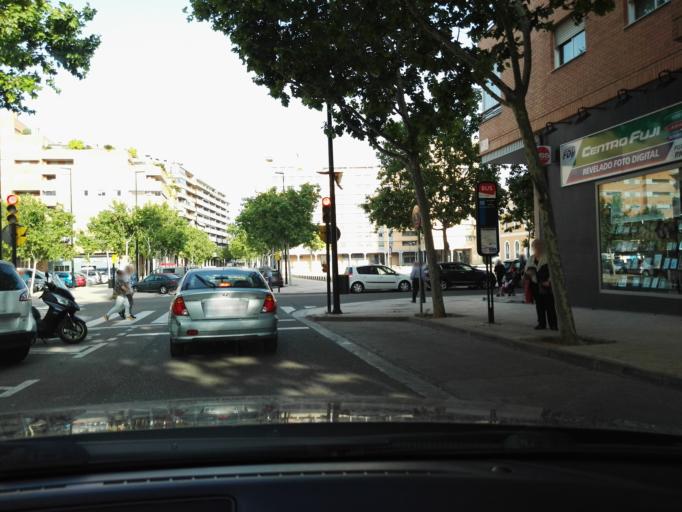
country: ES
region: Aragon
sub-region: Provincia de Zaragoza
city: Zaragoza
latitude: 41.6613
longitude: -0.8723
